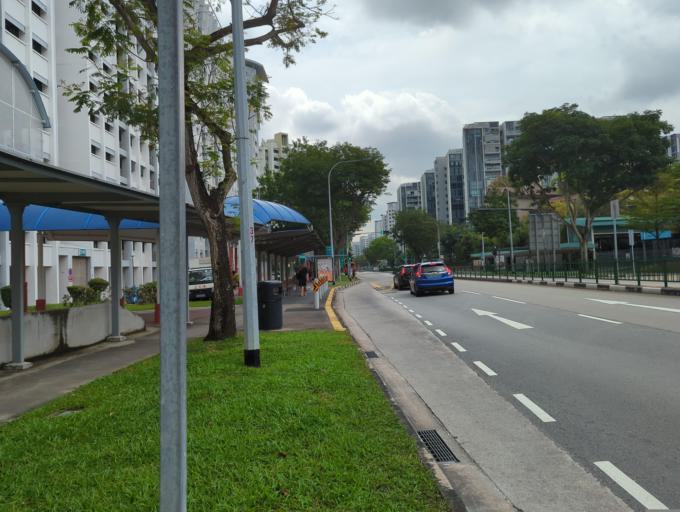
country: MY
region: Johor
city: Kampung Pasir Gudang Baru
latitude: 1.3913
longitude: 103.8978
